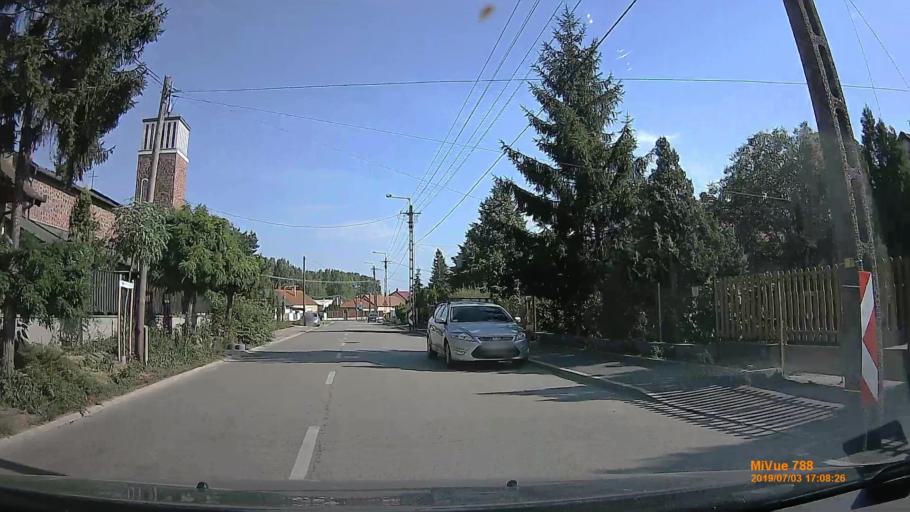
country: HU
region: Gyor-Moson-Sopron
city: Gyor
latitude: 47.7144
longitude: 17.6516
